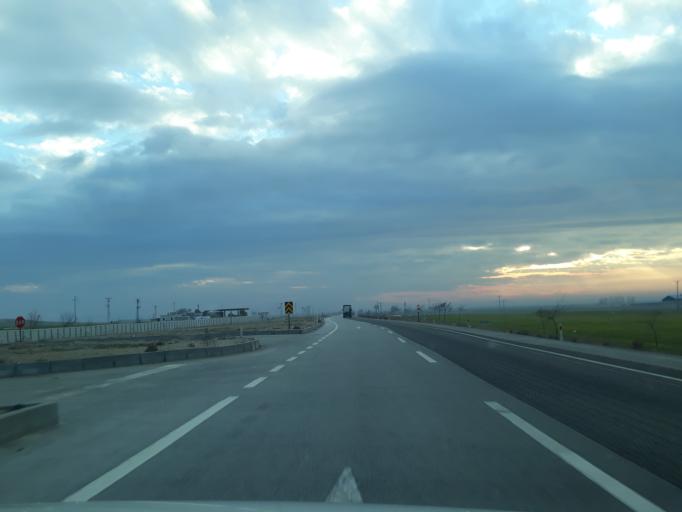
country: TR
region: Konya
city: Hotamis
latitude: 37.7105
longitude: 33.2757
